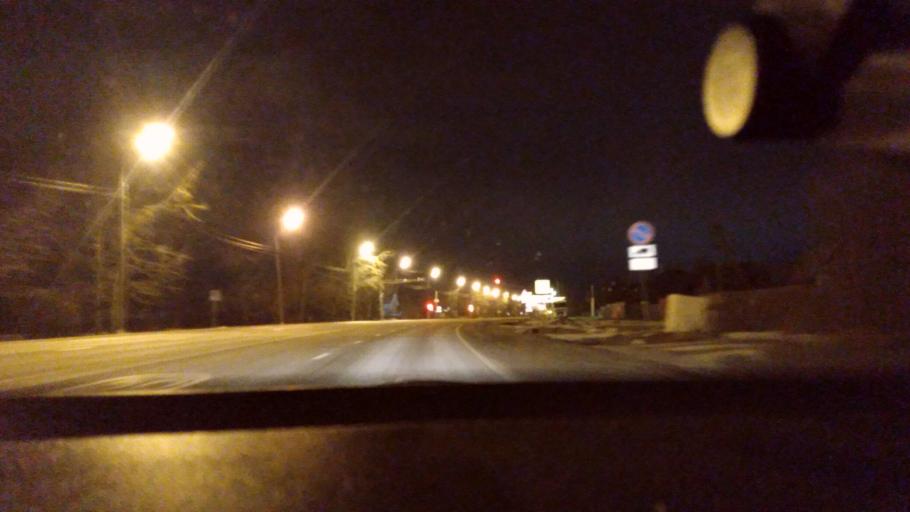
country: RU
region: Moskovskaya
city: Bronnitsy
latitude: 55.3853
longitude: 38.3493
